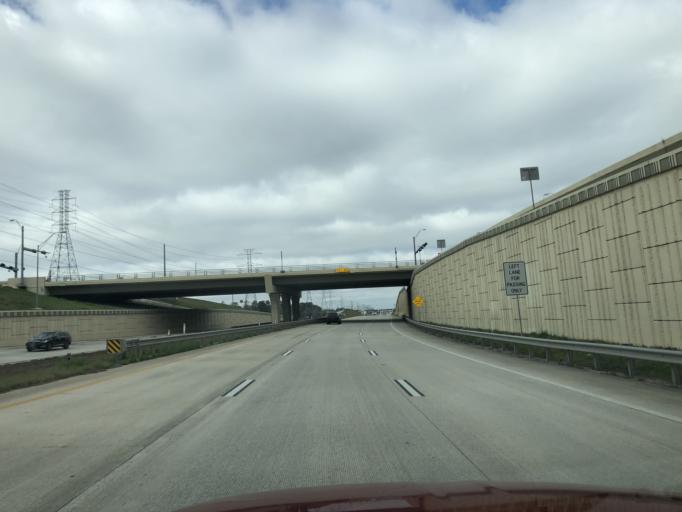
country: US
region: Texas
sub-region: Harris County
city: Spring
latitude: 30.0879
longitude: -95.4495
